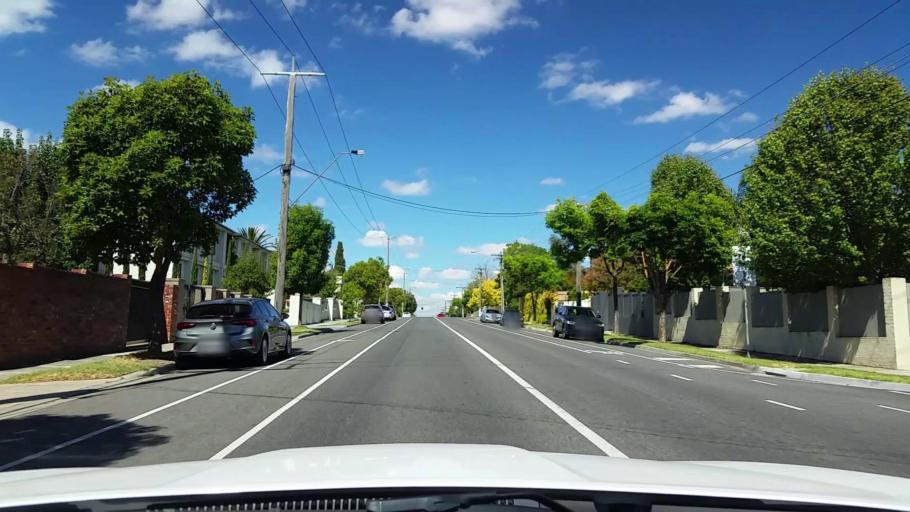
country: AU
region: Victoria
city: Carnegie
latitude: -37.8718
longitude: 145.0626
